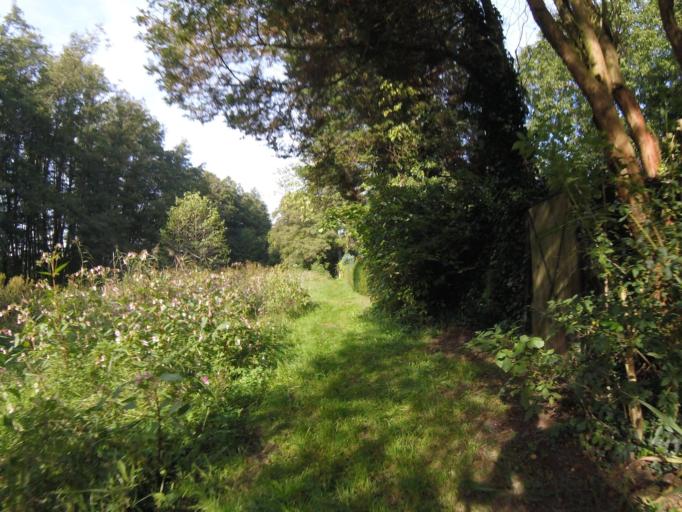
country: DE
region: Brandenburg
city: Bestensee
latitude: 52.2770
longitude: 13.6516
